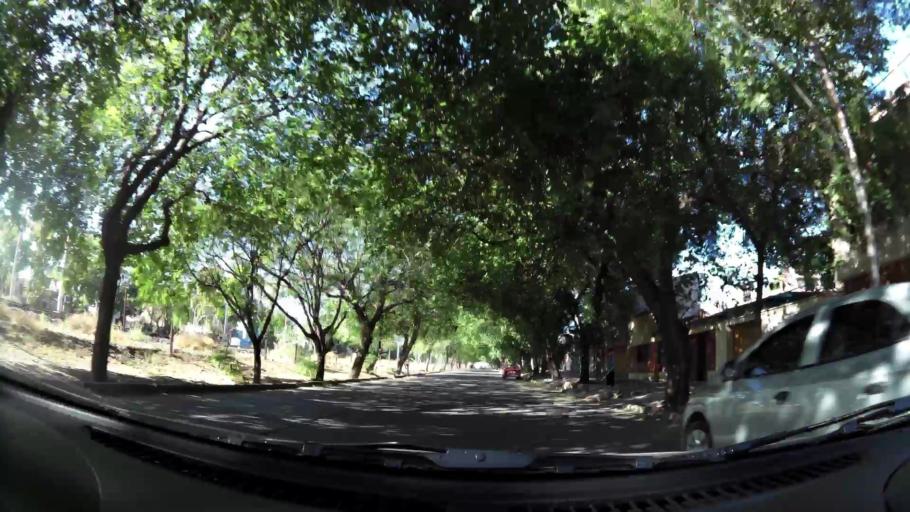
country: AR
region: Mendoza
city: Las Heras
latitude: -32.8715
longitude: -68.8455
